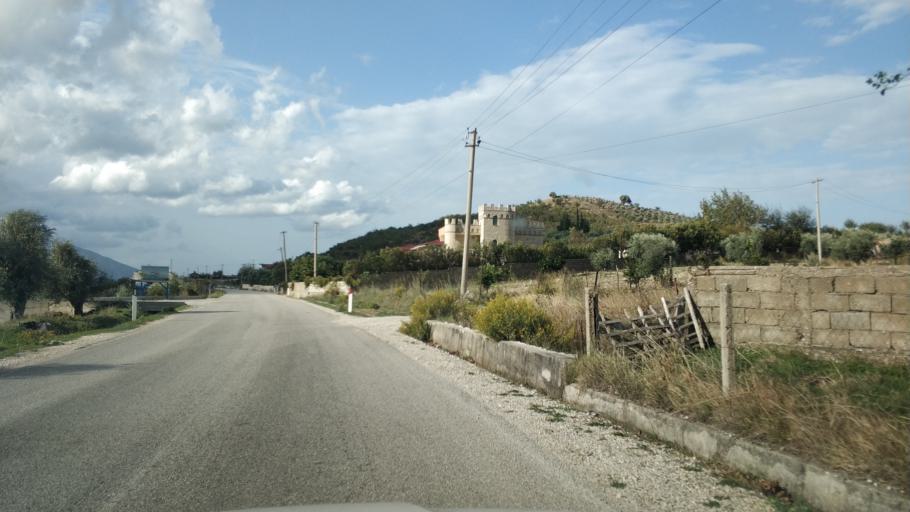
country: AL
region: Vlore
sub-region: Rrethi i Vlores
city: Orikum
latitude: 40.2958
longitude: 19.4902
